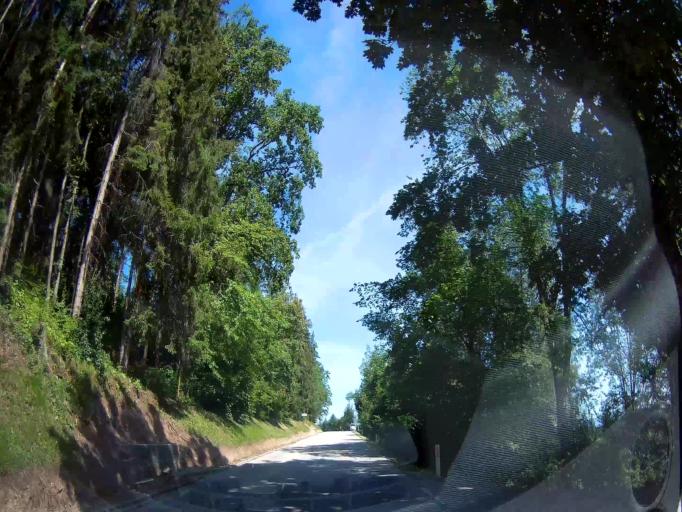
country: AT
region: Carinthia
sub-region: Politischer Bezirk Sankt Veit an der Glan
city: St. Georgen am Laengsee
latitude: 46.7883
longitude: 14.4192
